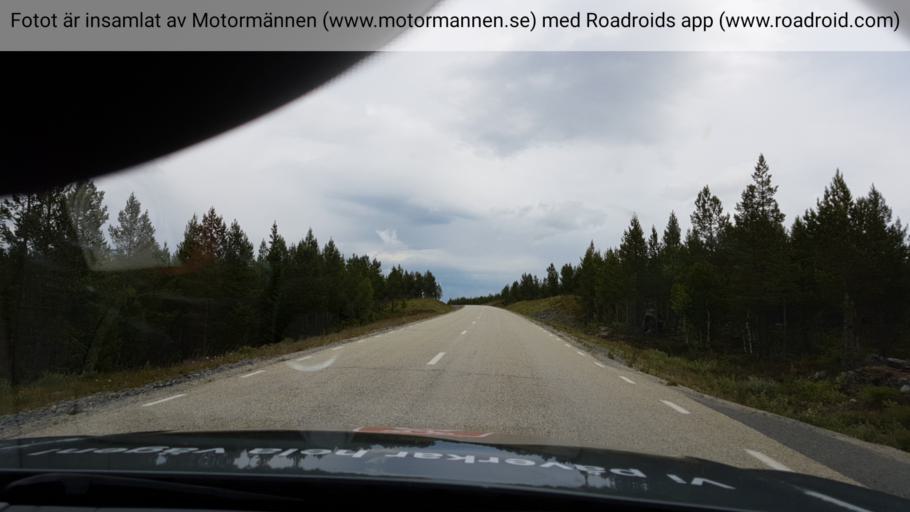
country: SE
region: Jaemtland
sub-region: Are Kommun
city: Jarpen
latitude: 62.8375
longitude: 13.2916
